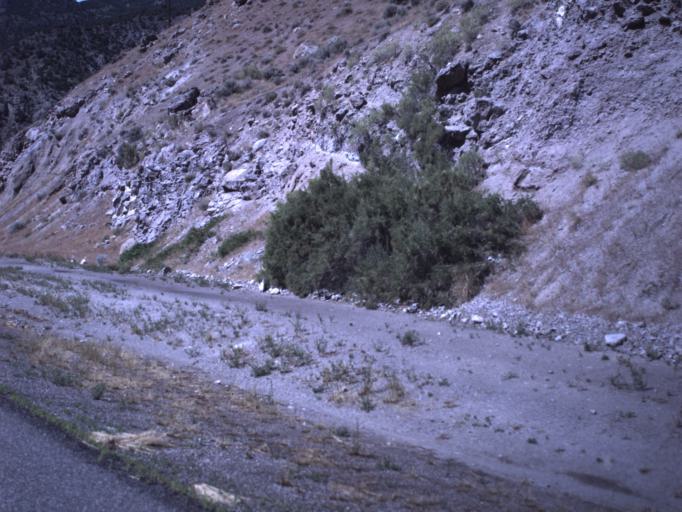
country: US
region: Utah
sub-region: Sevier County
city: Monroe
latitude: 38.5659
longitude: -112.2685
